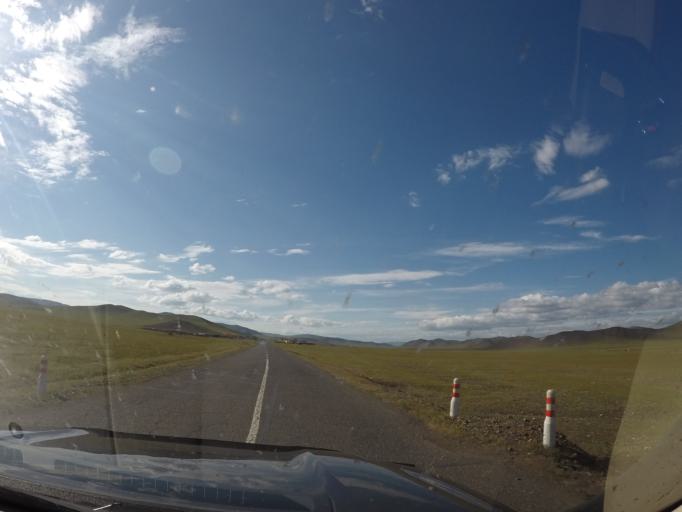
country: MN
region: Hentiy
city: Modot
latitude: 47.7189
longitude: 109.0386
